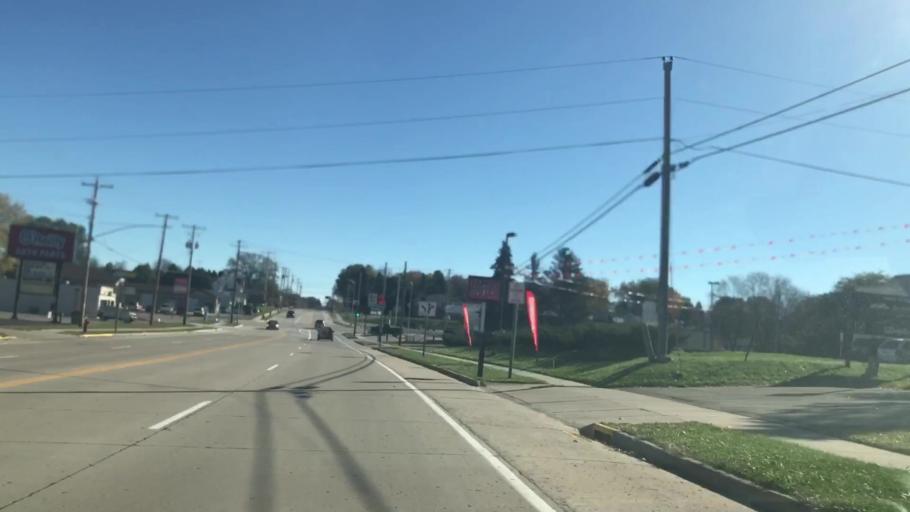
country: US
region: Wisconsin
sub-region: Dodge County
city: Mayville
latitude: 43.4940
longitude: -88.5583
